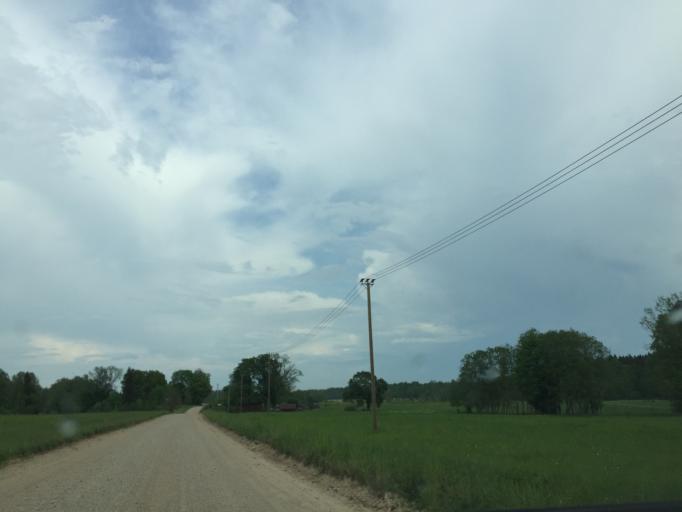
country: LV
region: Livani
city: Livani
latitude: 56.5599
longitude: 26.1236
